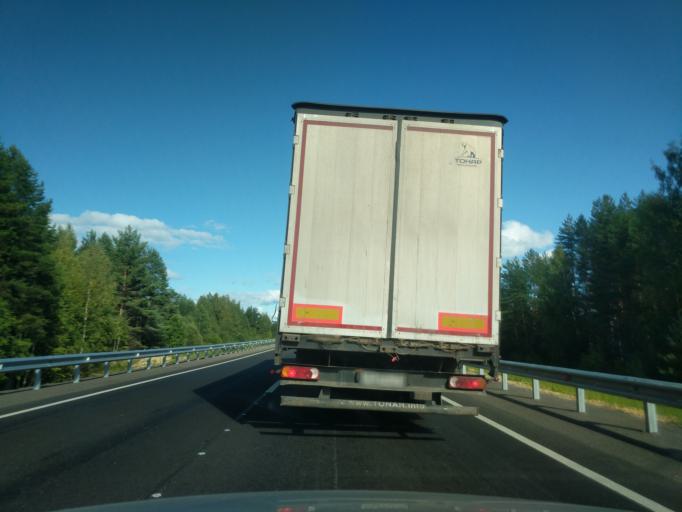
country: RU
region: Kostroma
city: Makar'yev
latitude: 57.8482
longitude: 43.6769
